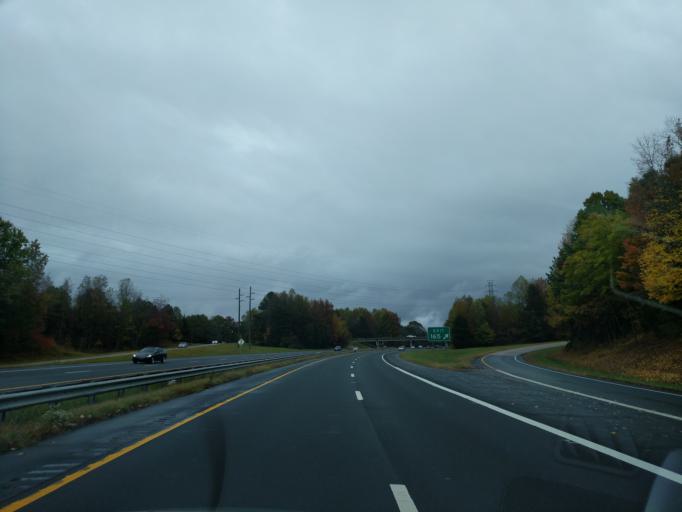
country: US
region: North Carolina
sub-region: Orange County
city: Hillsborough
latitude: 36.0586
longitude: -79.0872
